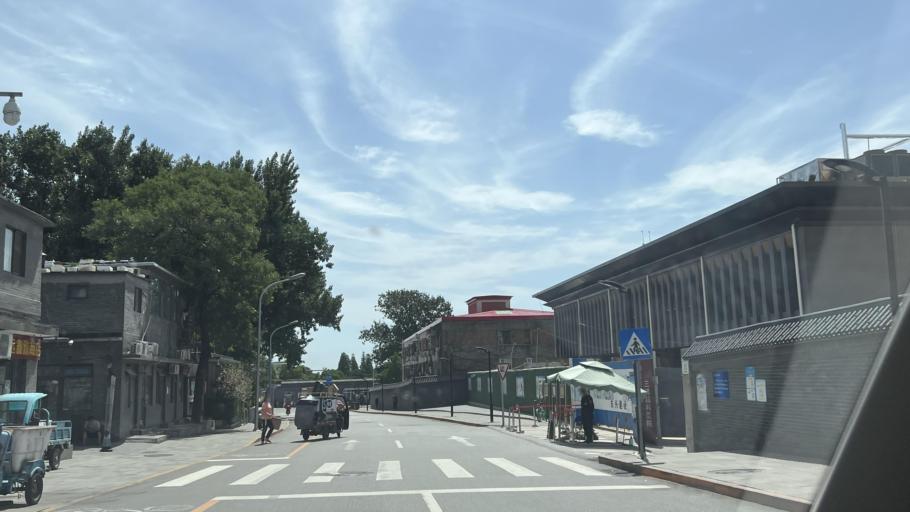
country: CN
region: Beijing
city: Xiangshan
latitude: 39.9916
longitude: 116.2024
